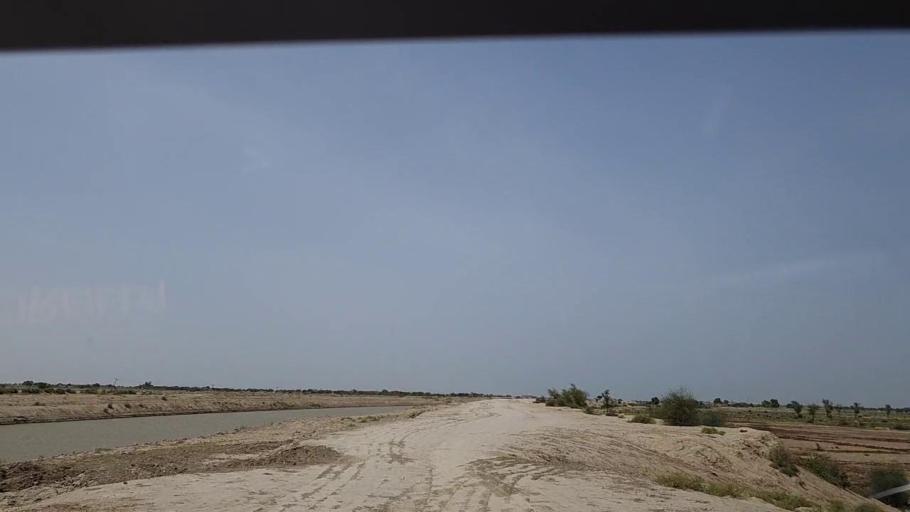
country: PK
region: Sindh
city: Johi
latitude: 26.7321
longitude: 67.6828
